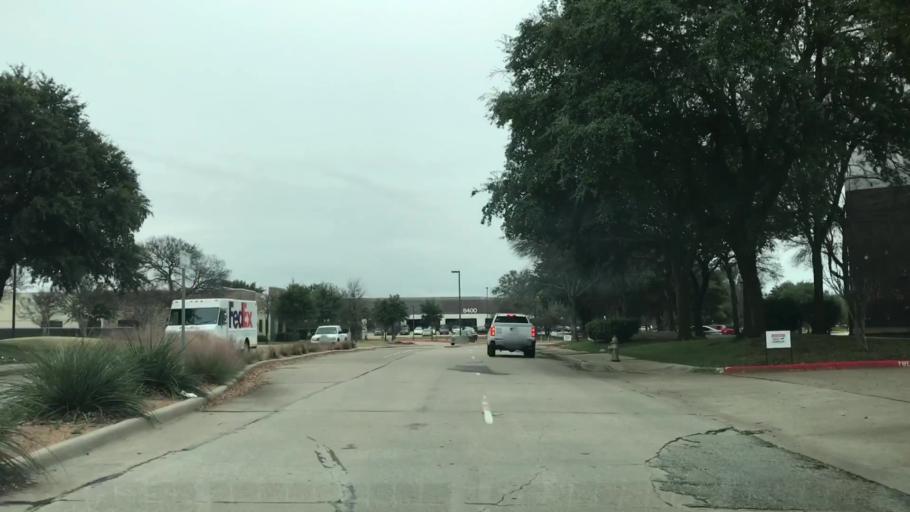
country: US
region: Texas
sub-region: Dallas County
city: Coppell
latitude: 32.9257
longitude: -97.0087
